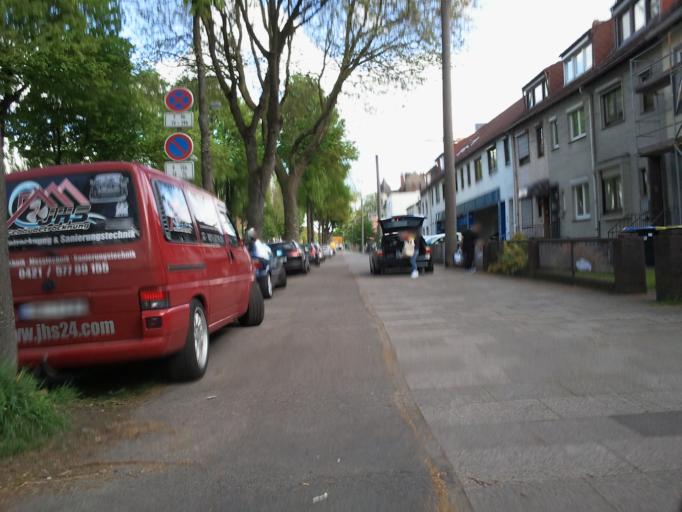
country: DE
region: Lower Saxony
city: Ritterhude
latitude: 53.1350
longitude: 8.7318
